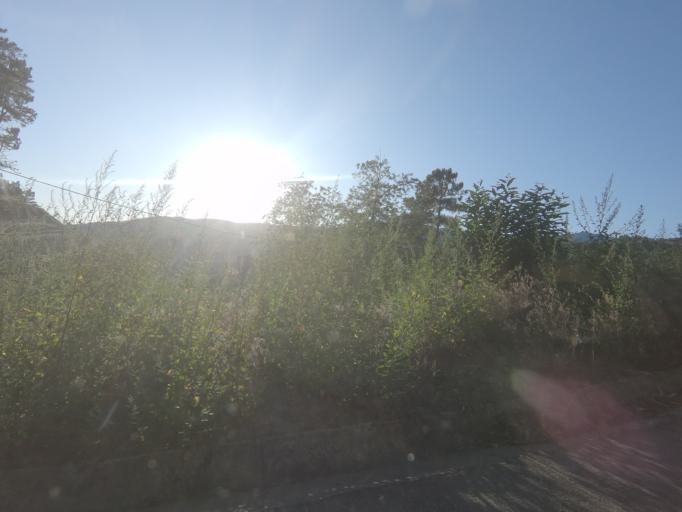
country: PT
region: Vila Real
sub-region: Peso da Regua
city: Godim
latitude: 41.1893
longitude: -7.8295
